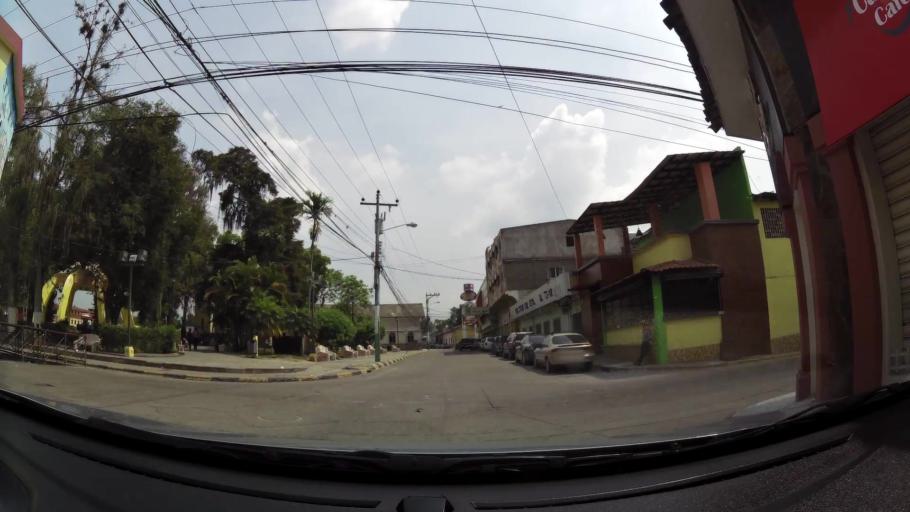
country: HN
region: Comayagua
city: Siguatepeque
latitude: 14.5961
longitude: -87.8280
